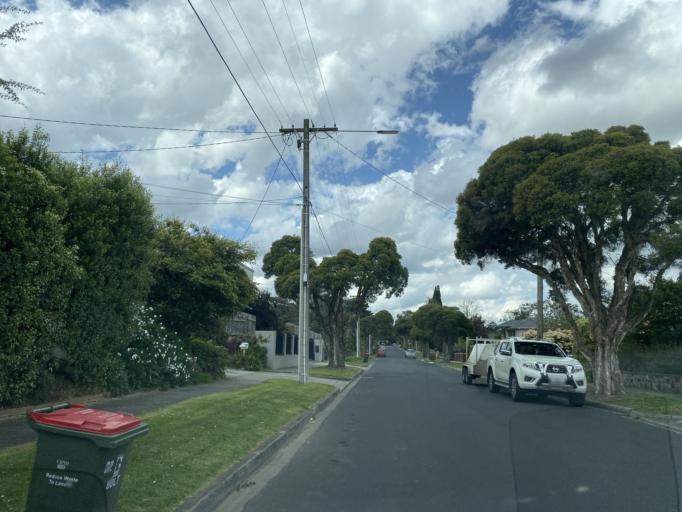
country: AU
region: Victoria
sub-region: Whitehorse
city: Burwood
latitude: -37.8539
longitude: 145.1286
